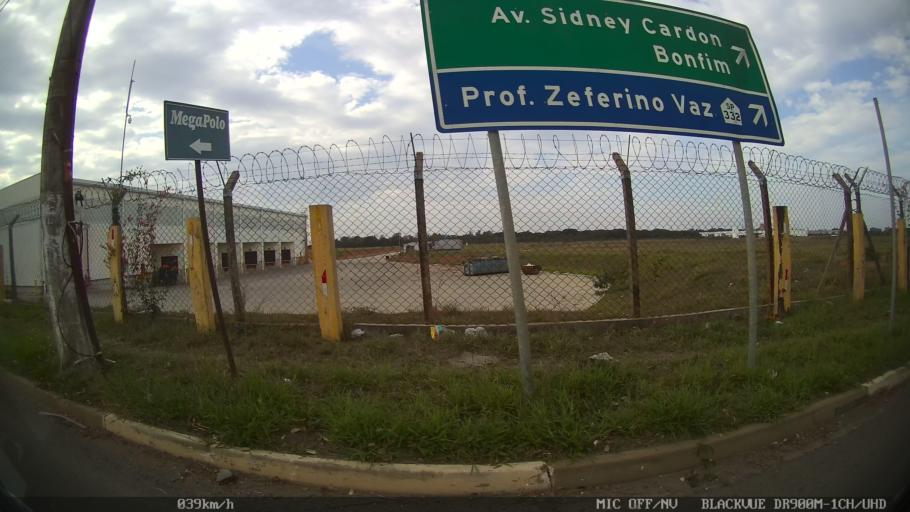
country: BR
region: Sao Paulo
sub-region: Paulinia
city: Paulinia
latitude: -22.7303
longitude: -47.1664
